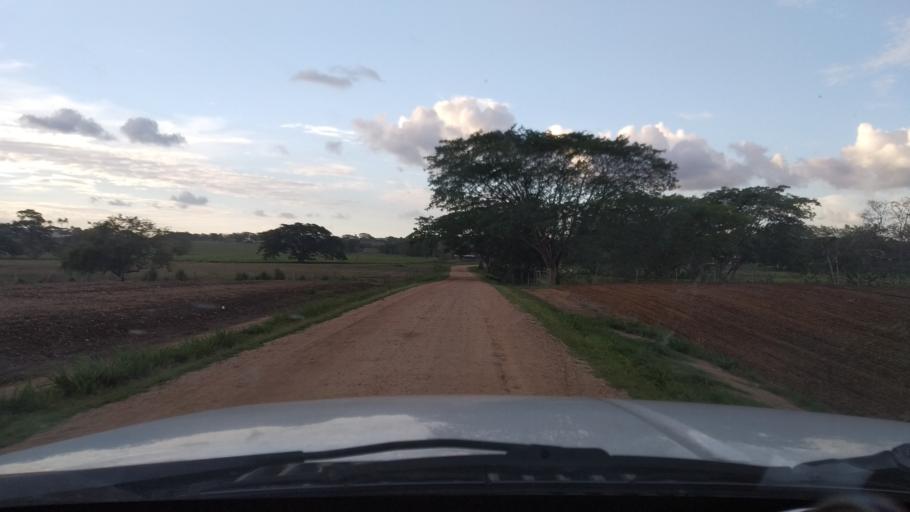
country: BZ
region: Cayo
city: San Ignacio
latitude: 17.2211
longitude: -88.9984
